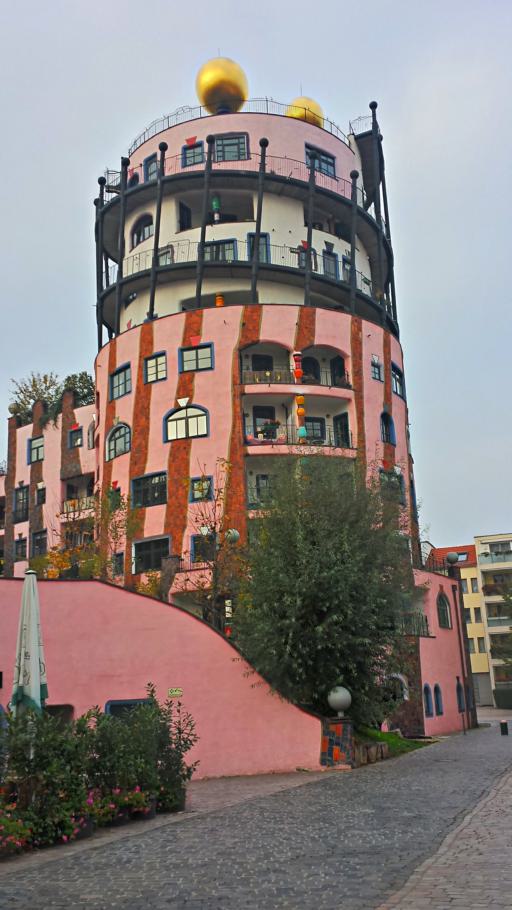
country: DE
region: Saxony-Anhalt
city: Magdeburg
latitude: 52.1267
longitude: 11.6347
